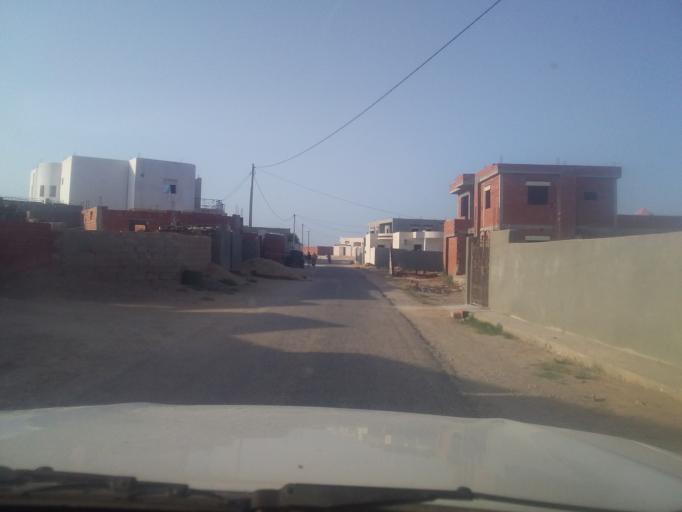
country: TN
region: Qabis
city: Gabes
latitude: 33.6355
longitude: 10.2882
